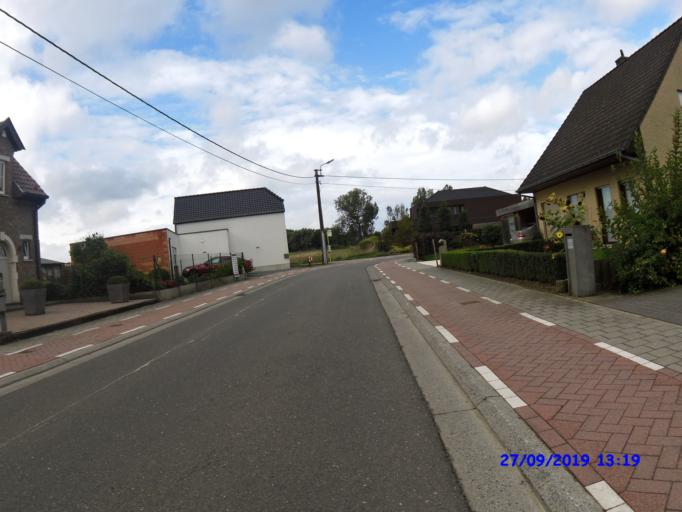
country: BE
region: Flanders
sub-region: Provincie Oost-Vlaanderen
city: Lede
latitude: 50.9536
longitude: 3.9463
